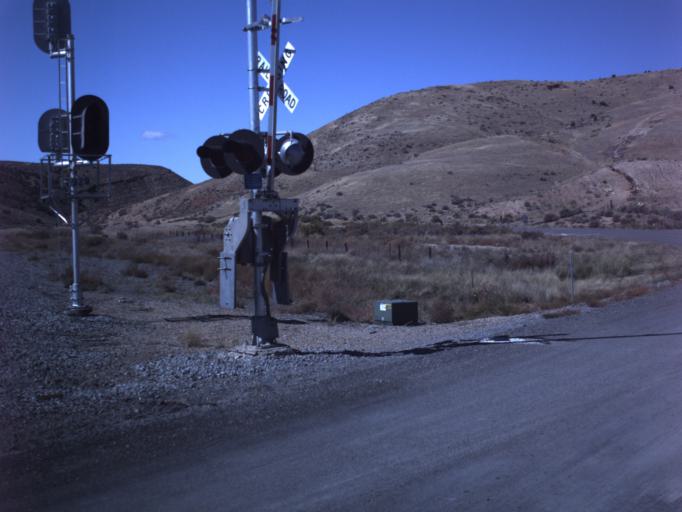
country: US
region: Utah
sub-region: Juab County
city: Nephi
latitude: 39.4858
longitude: -111.9822
